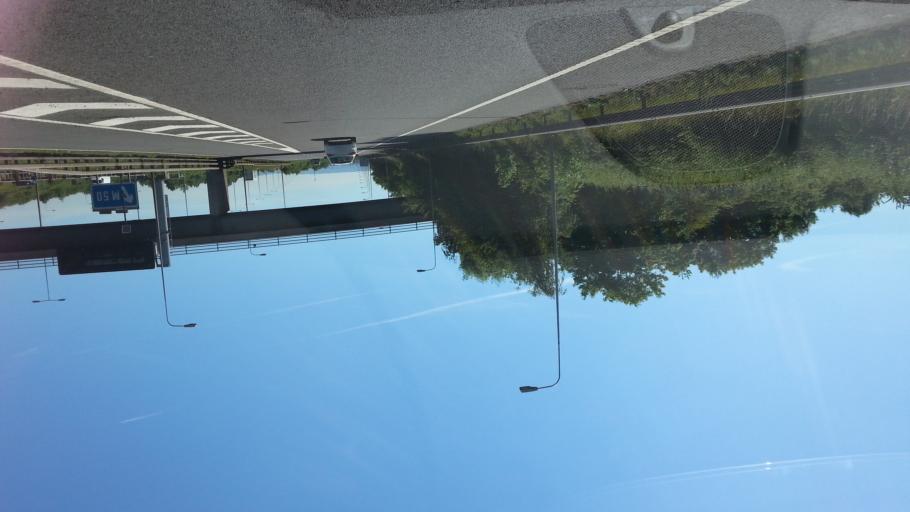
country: GB
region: England
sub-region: Worcestershire
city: Bredon
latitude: 52.0535
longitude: -2.1384
